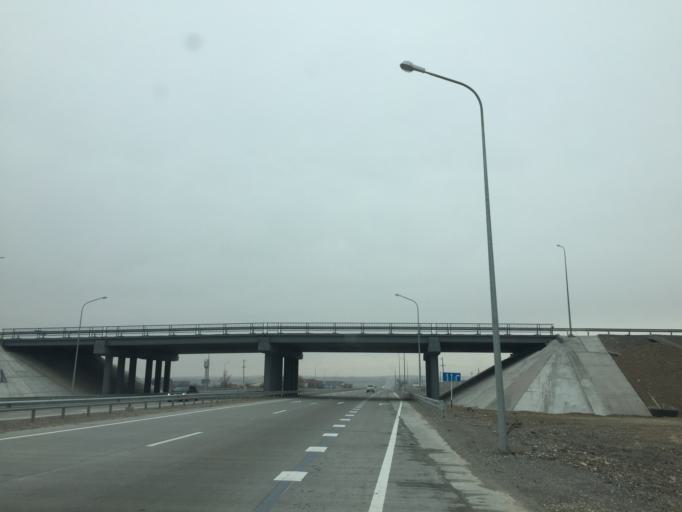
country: KZ
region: Ongtustik Qazaqstan
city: Aksu
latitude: 42.4734
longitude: 69.8139
